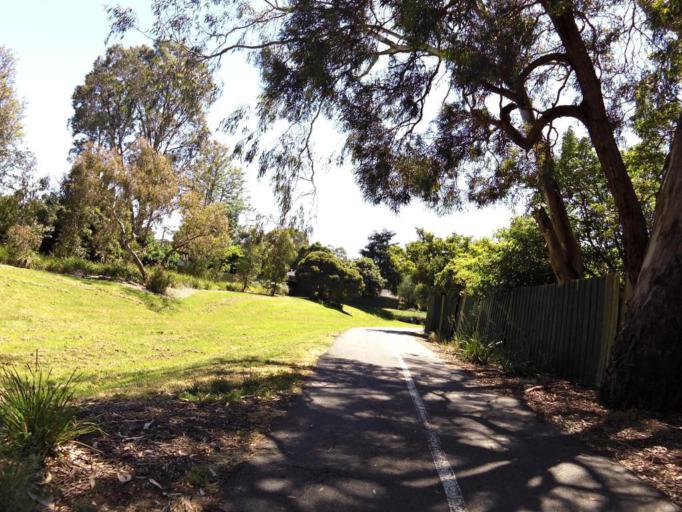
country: AU
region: Victoria
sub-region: Knox
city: Boronia
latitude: -37.8734
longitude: 145.2890
